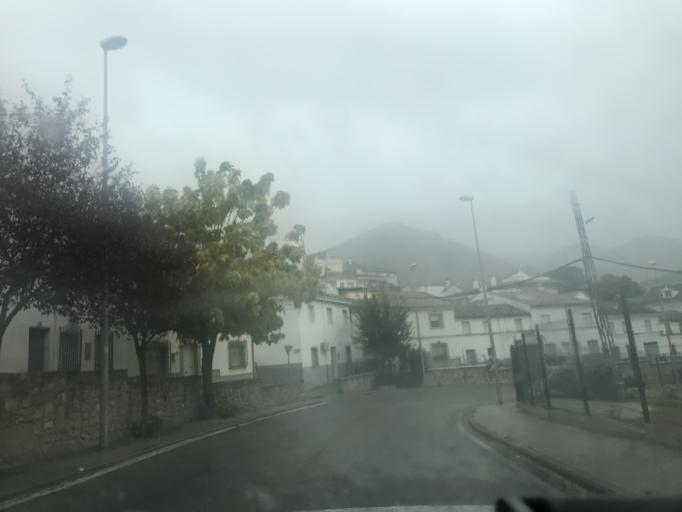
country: ES
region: Andalusia
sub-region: Provincia de Jaen
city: Cazorla
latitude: 37.9177
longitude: -3.0060
